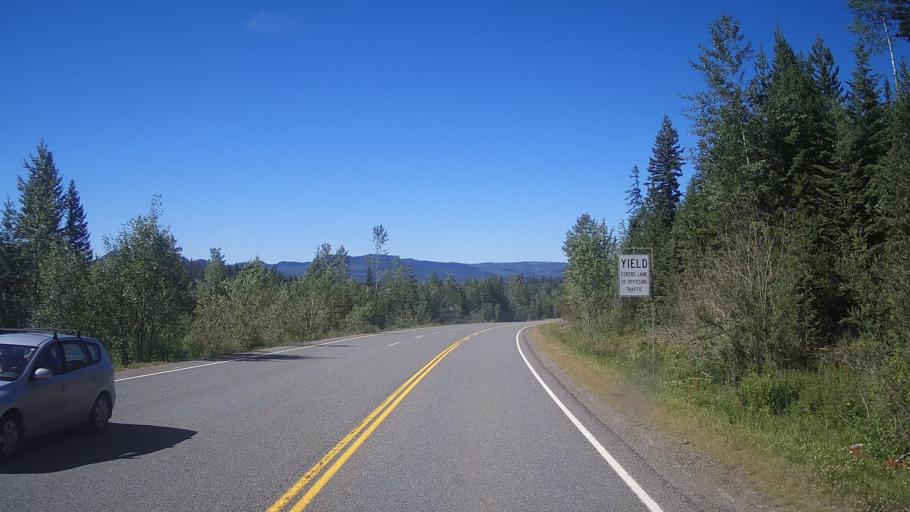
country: CA
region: British Columbia
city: Kamloops
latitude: 51.4938
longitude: -120.4536
